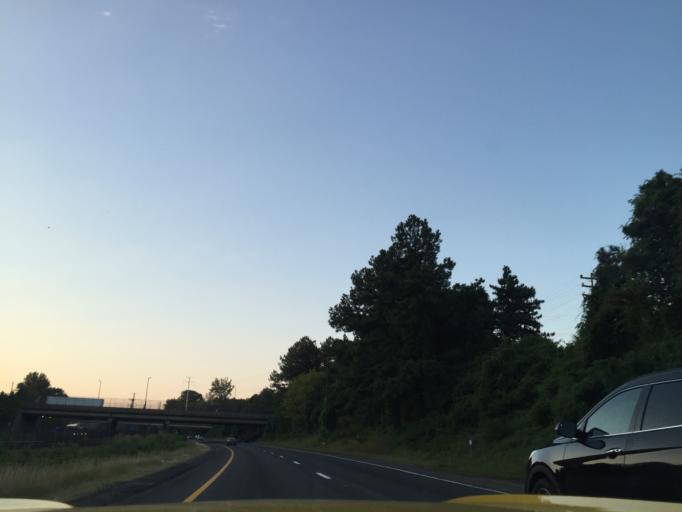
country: US
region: Virginia
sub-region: City of Falls Church
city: Falls Church
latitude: 38.8890
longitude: -77.1634
